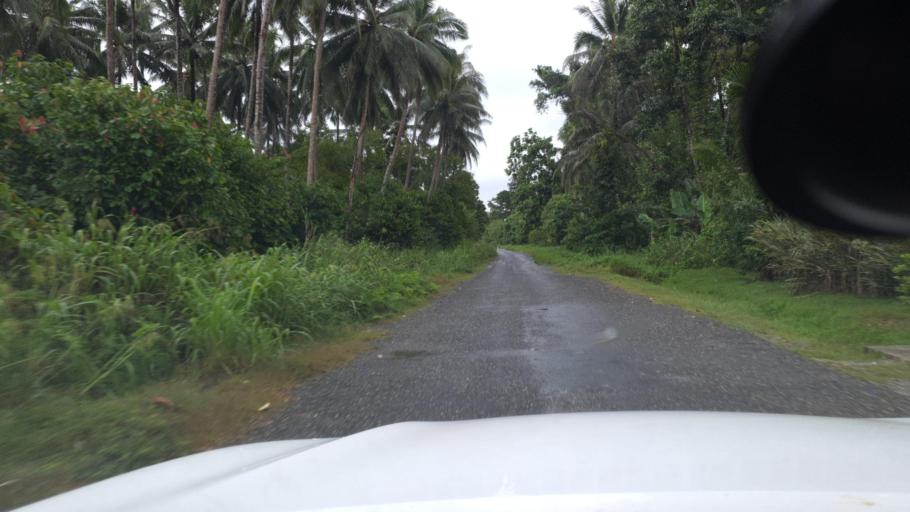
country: SB
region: Guadalcanal
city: Honiara
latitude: -9.4714
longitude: 160.3601
